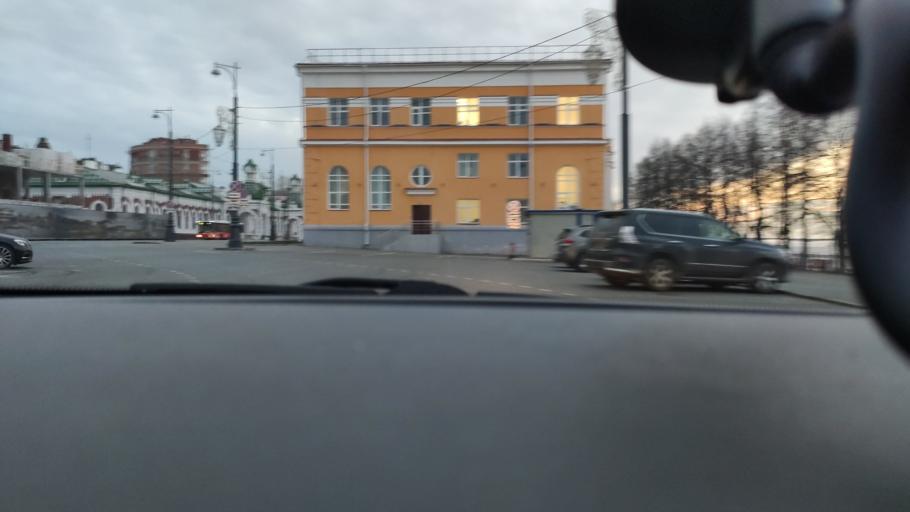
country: RU
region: Perm
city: Perm
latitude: 58.0212
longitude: 56.2532
